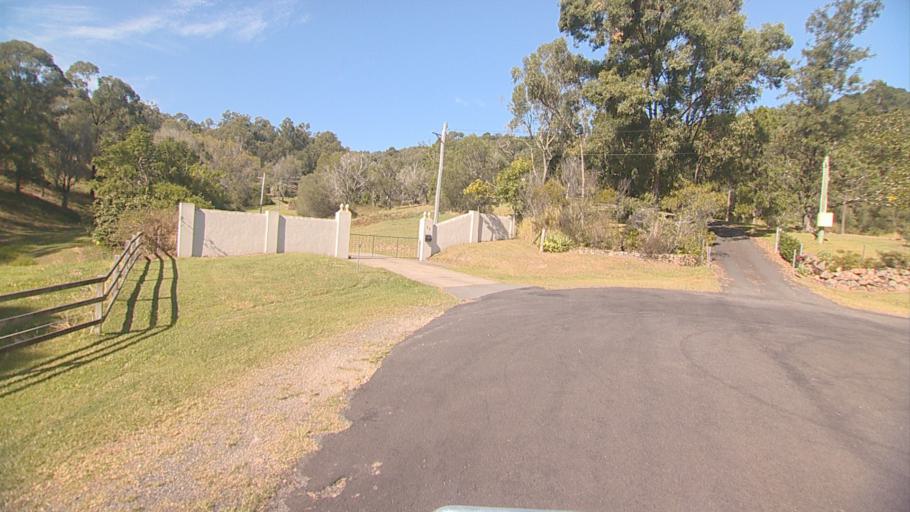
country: AU
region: Queensland
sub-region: Logan
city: Windaroo
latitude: -27.7446
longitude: 153.1722
